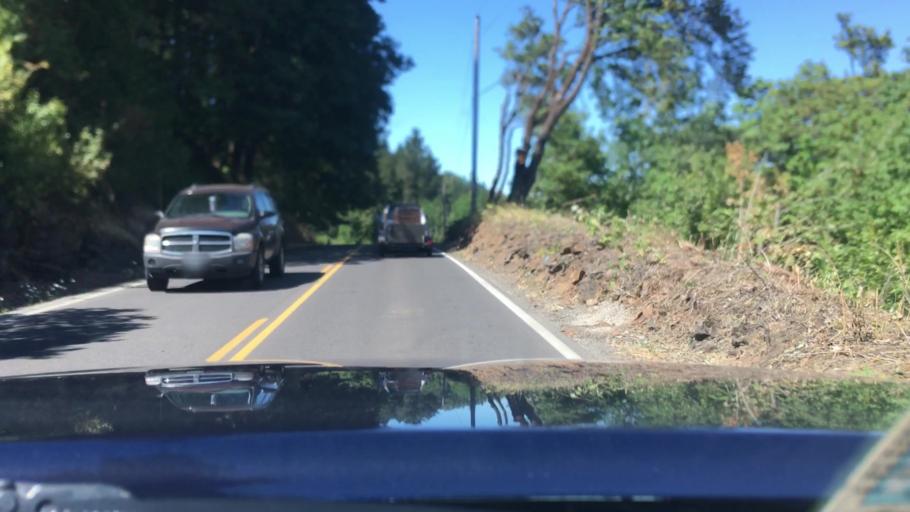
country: US
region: Oregon
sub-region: Lane County
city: Cottage Grove
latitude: 43.8181
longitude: -123.0460
